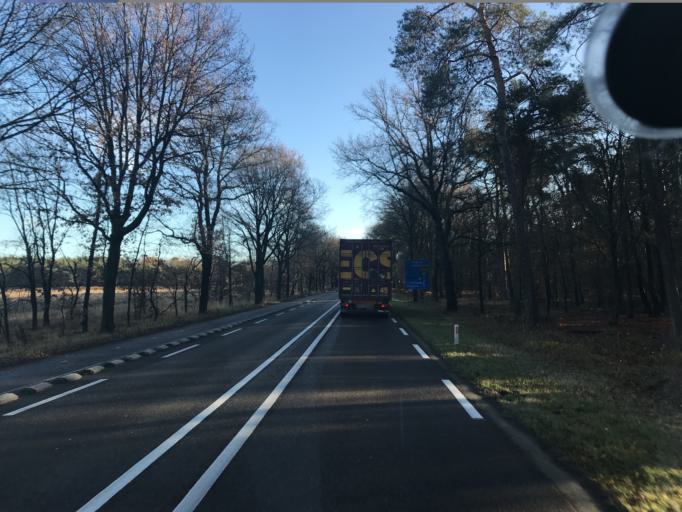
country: NL
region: Gelderland
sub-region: Gemeente Ermelo
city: Ermelo
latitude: 52.3101
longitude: 5.6788
